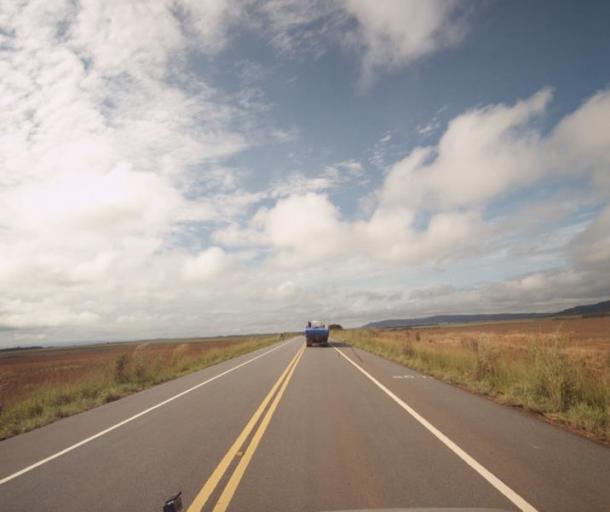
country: BR
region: Goias
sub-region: Barro Alto
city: Barro Alto
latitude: -15.2717
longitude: -48.6847
